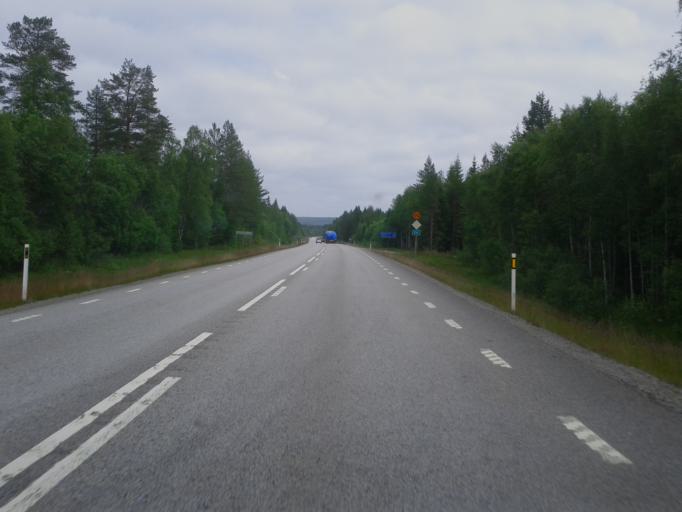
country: SE
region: Vaesterbotten
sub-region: Robertsfors Kommun
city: Robertsfors
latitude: 64.2820
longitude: 21.0667
